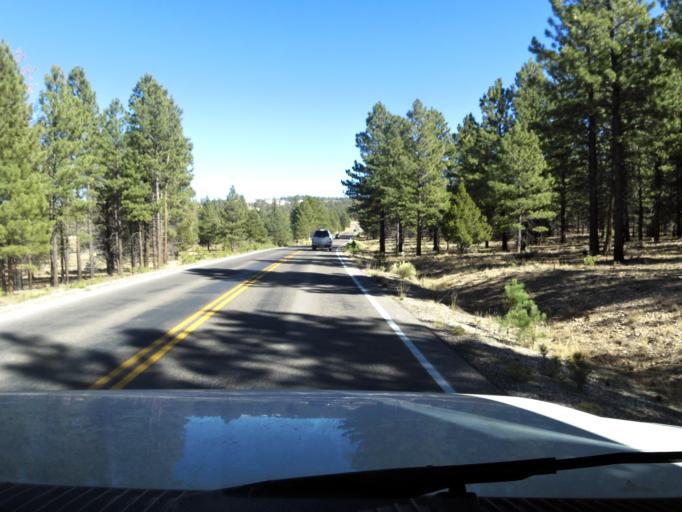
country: US
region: Utah
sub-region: Garfield County
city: Panguitch
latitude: 37.6070
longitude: -112.1969
